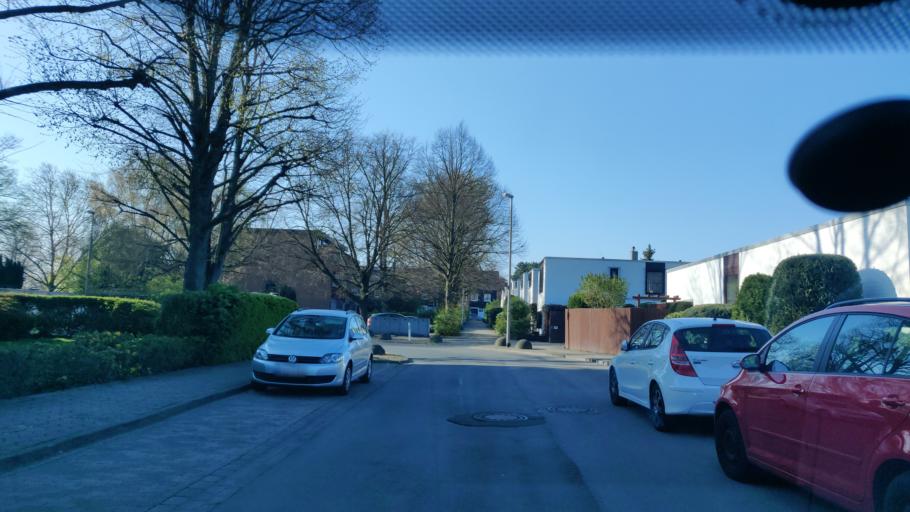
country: DE
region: Lower Saxony
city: Laatzen
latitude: 52.3529
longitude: 9.8362
